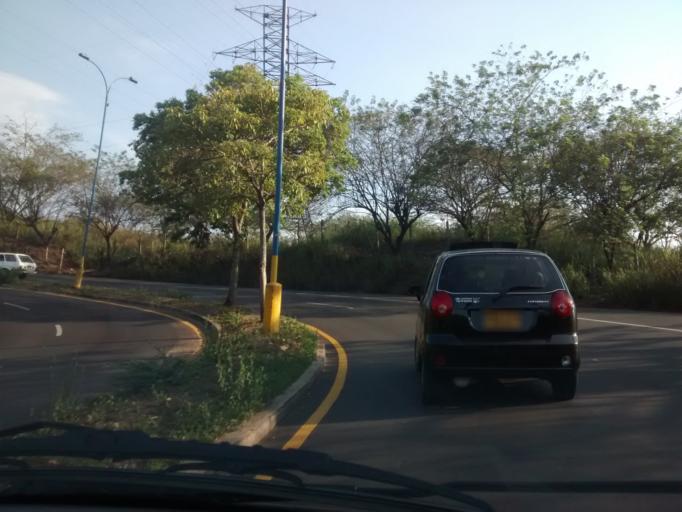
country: CO
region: Santander
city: Bucaramanga
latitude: 7.0905
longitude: -73.1316
